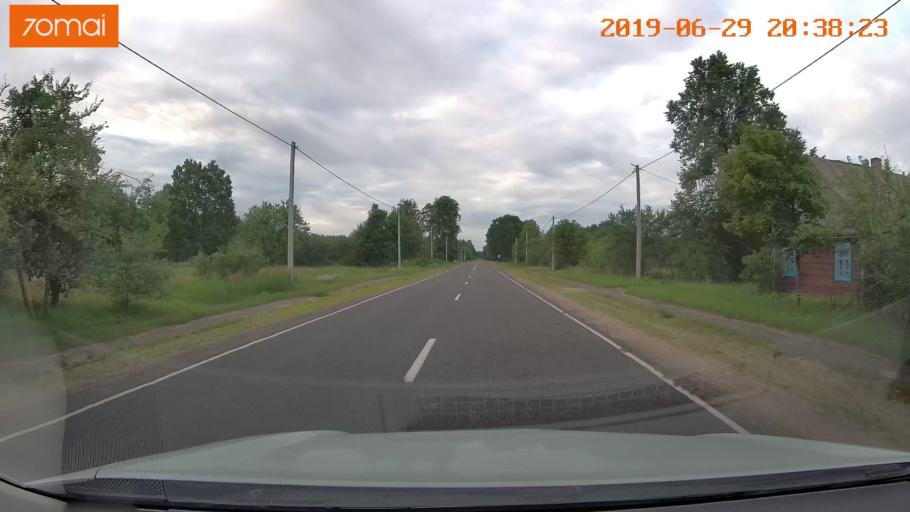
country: BY
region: Brest
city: Hantsavichy
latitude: 52.5494
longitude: 26.3647
